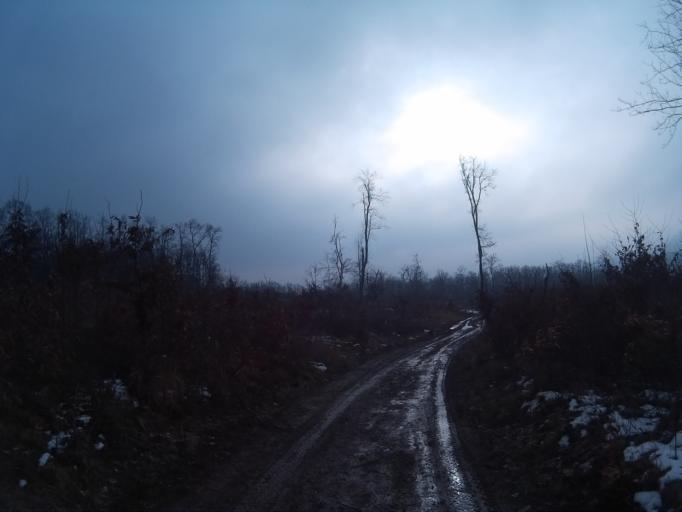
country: HU
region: Komarom-Esztergom
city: Labatlan
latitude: 47.6920
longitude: 18.5206
